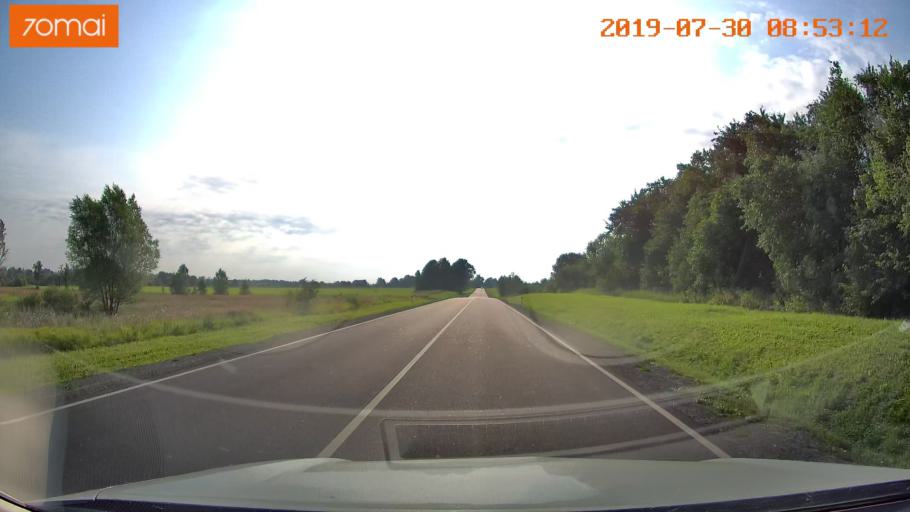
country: RU
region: Kaliningrad
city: Chernyakhovsk
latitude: 54.6020
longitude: 21.9918
